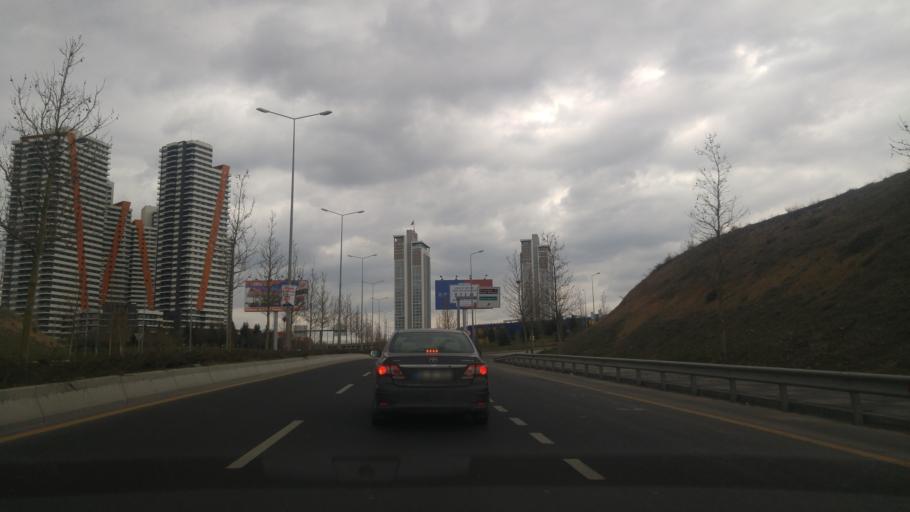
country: TR
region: Ankara
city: Mamak
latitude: 39.8870
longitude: 32.9273
